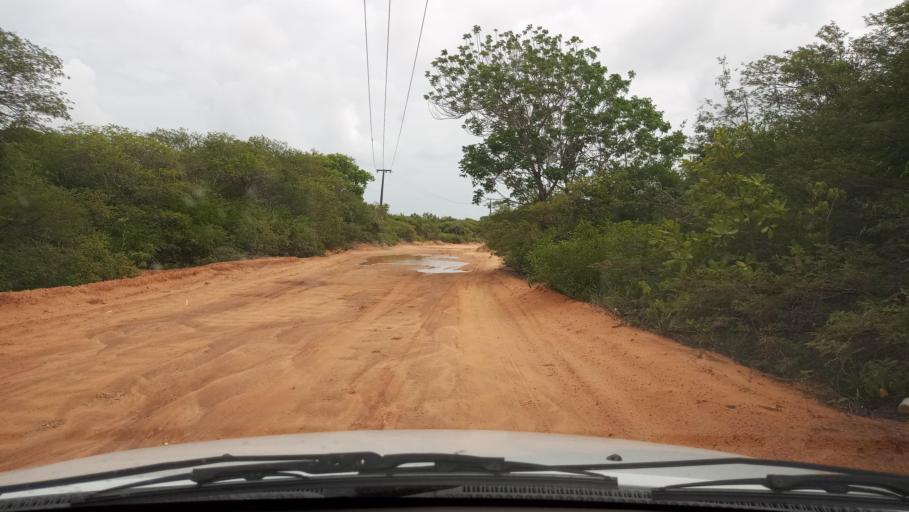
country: BR
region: Rio Grande do Norte
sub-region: Maxaranguape
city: Sao Miguel
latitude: -5.4729
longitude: -35.3011
